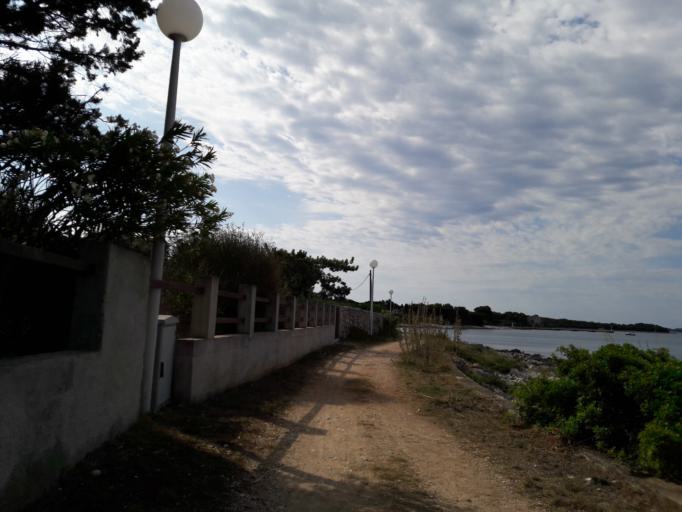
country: HR
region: Licko-Senjska
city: Novalja
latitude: 44.3792
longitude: 14.6897
